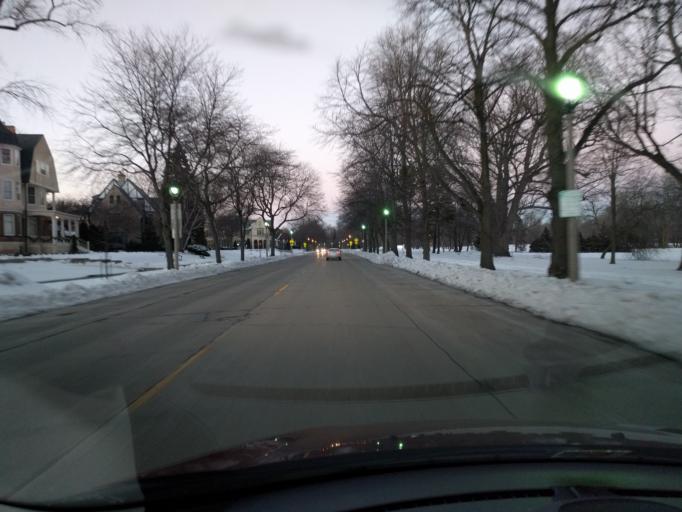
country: US
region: Wisconsin
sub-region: Milwaukee County
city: Shorewood
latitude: 43.0679
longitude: -87.8733
